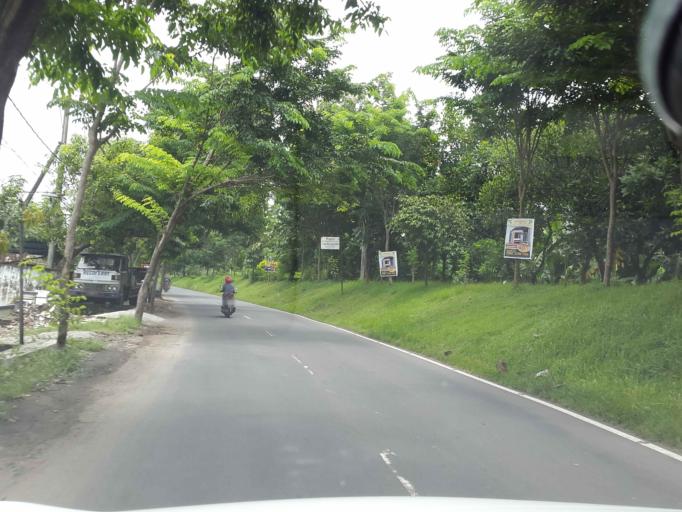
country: ID
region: East Java
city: Mojokerto
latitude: -7.4597
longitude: 112.4268
